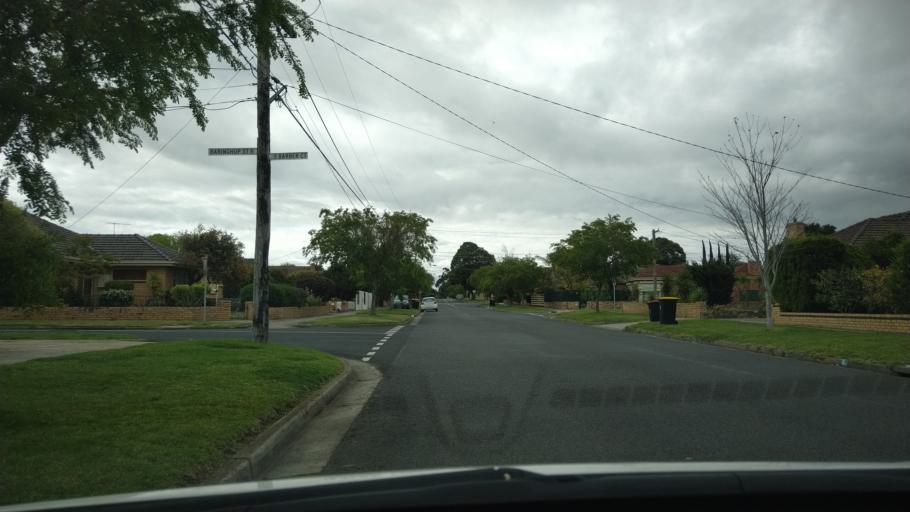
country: AU
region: Victoria
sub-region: Bayside
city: Cheltenham
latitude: -37.9657
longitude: 145.0649
